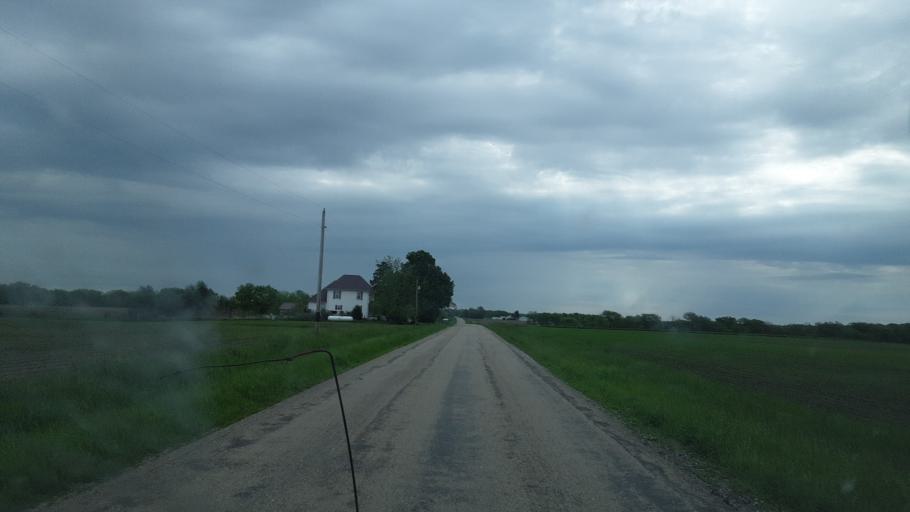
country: US
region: Illinois
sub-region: Fulton County
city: Astoria
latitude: 40.3646
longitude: -90.4714
